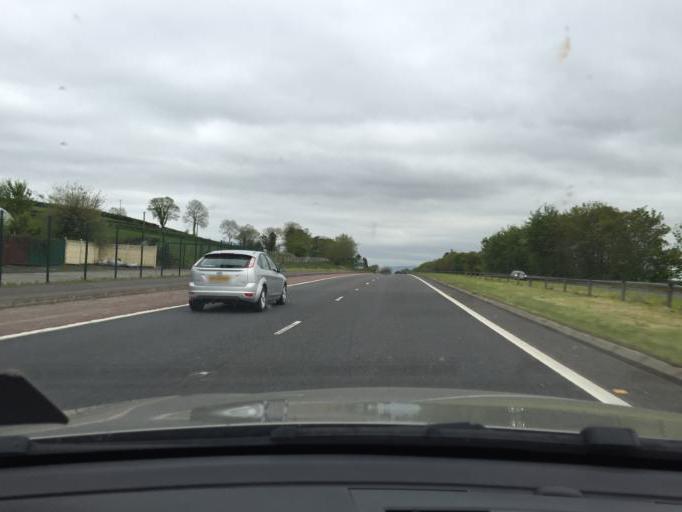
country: GB
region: Northern Ireland
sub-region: Banbridge District
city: Banbridge
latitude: 54.2718
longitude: -6.3095
